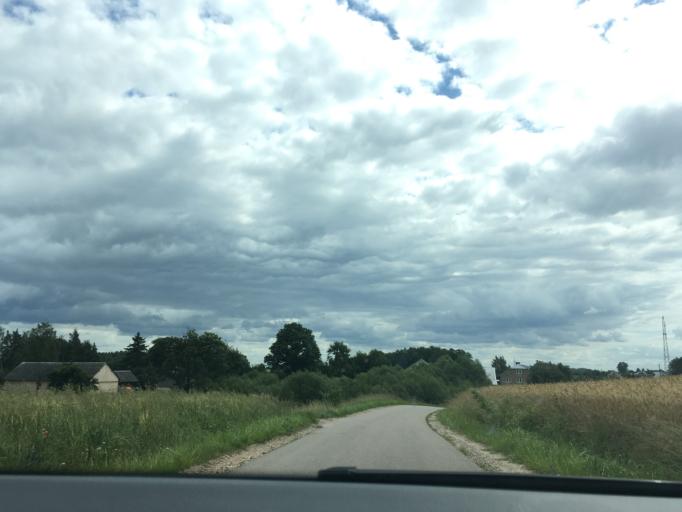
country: PL
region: Podlasie
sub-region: Powiat sejnenski
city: Sejny
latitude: 54.1038
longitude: 23.2798
